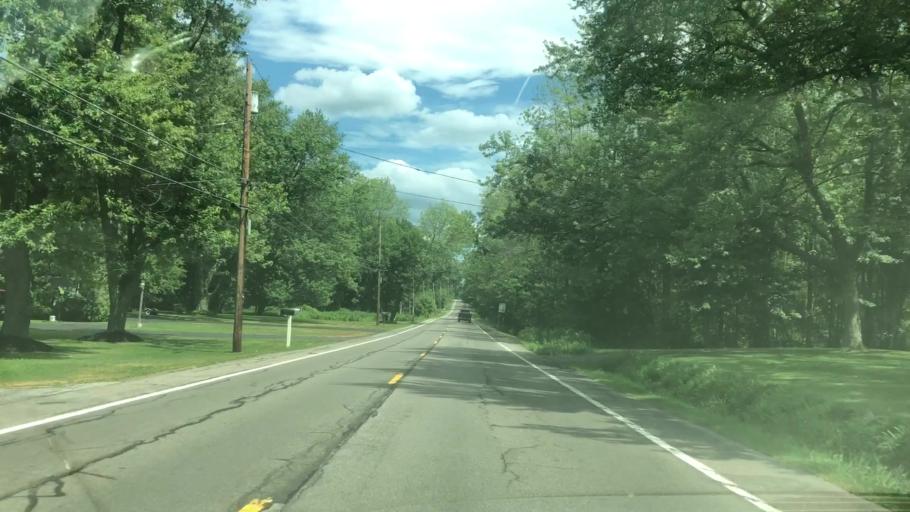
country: US
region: New York
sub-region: Monroe County
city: Webster
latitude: 43.1599
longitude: -77.4282
